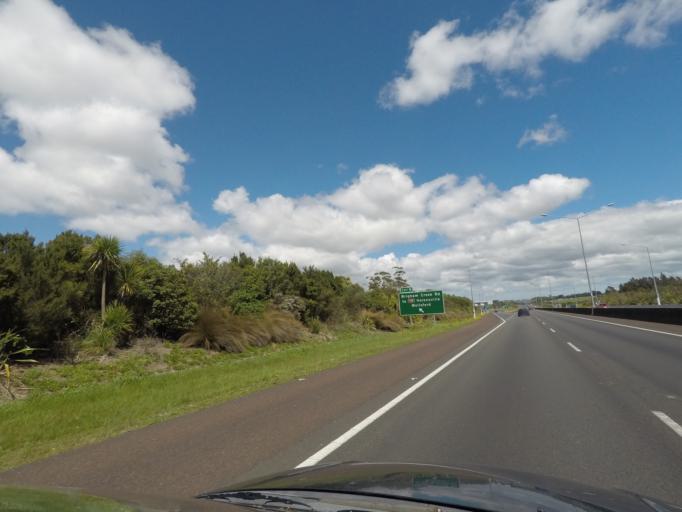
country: NZ
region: Auckland
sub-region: Auckland
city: Rosebank
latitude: -36.7970
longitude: 174.6439
